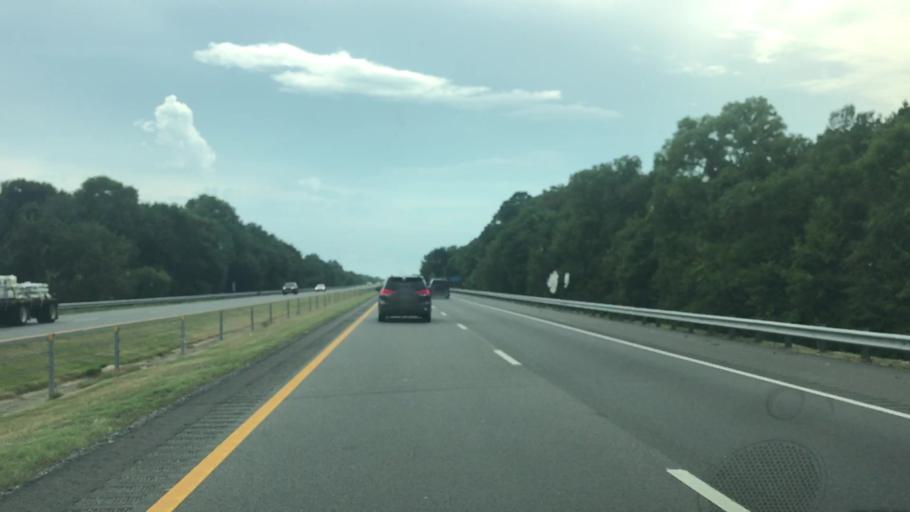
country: US
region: Arkansas
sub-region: Monroe County
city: Brinkley
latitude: 34.8895
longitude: -91.2539
